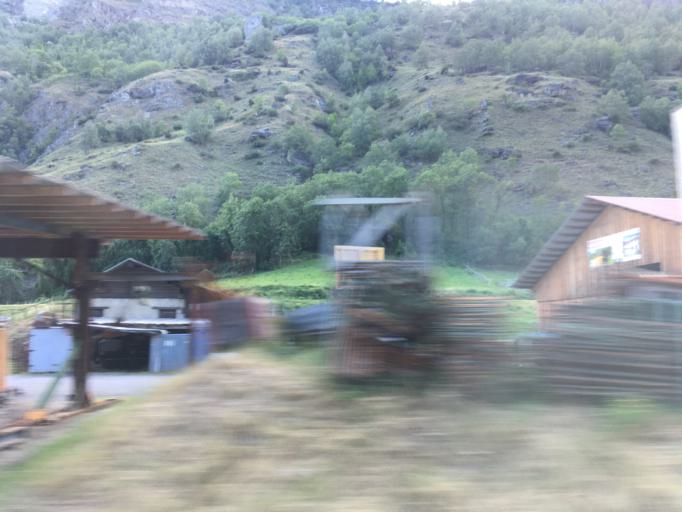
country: CH
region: Valais
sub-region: Brig District
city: Naters
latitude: 46.3496
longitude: 8.0372
